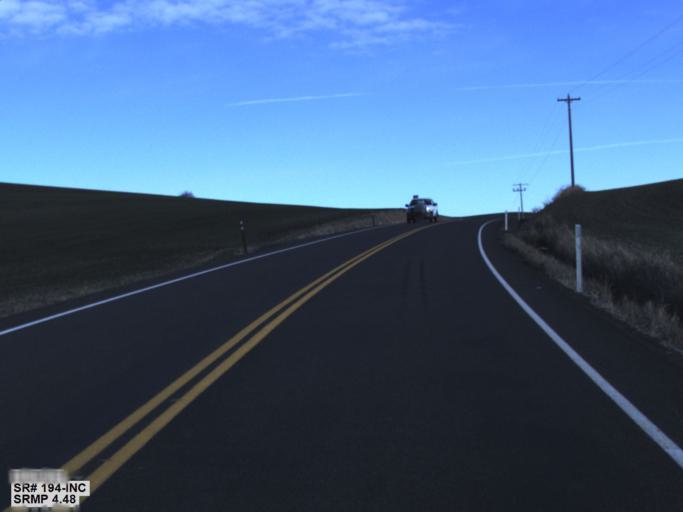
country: US
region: Washington
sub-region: Whitman County
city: Colfax
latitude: 46.7366
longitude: -117.4840
